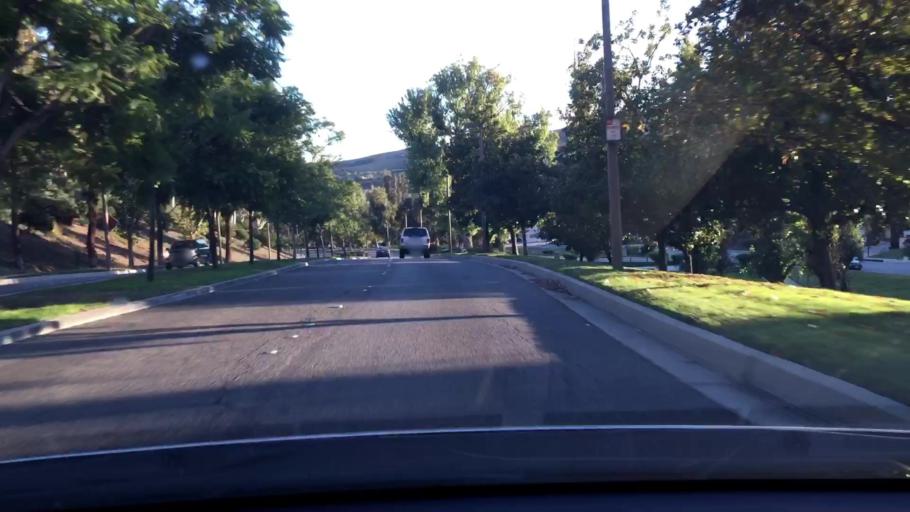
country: US
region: California
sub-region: Los Angeles County
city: Pomona
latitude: 34.0332
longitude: -117.7770
